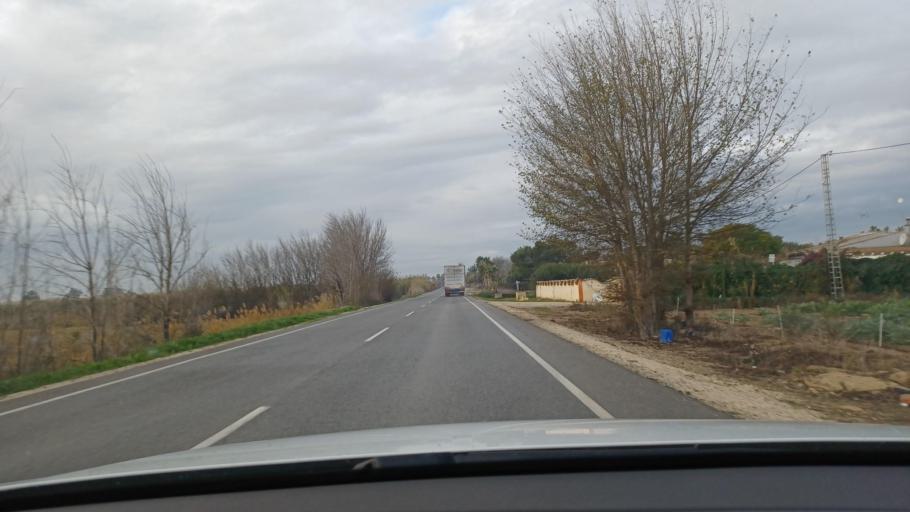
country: ES
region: Valencia
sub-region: Provincia de Alicante
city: Daya Vieja
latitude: 38.1522
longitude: -0.7137
